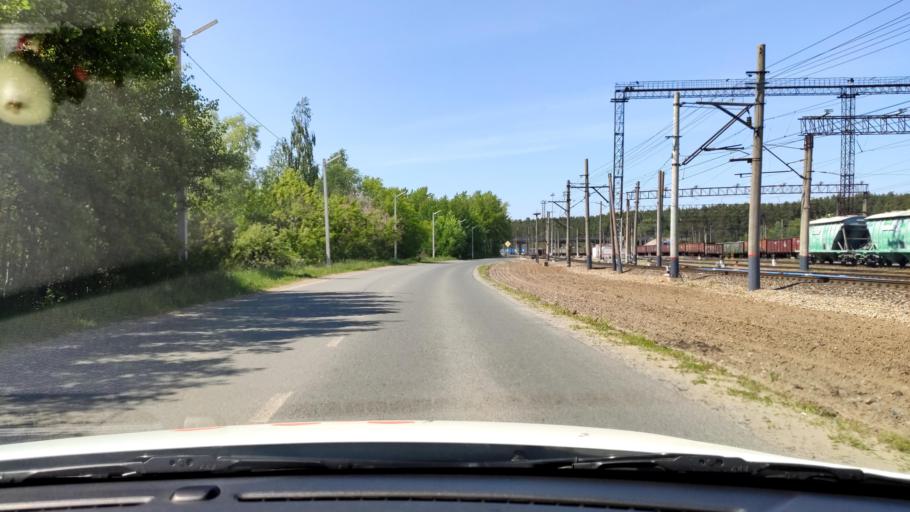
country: RU
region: Tatarstan
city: Osinovo
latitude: 55.8220
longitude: 48.8523
